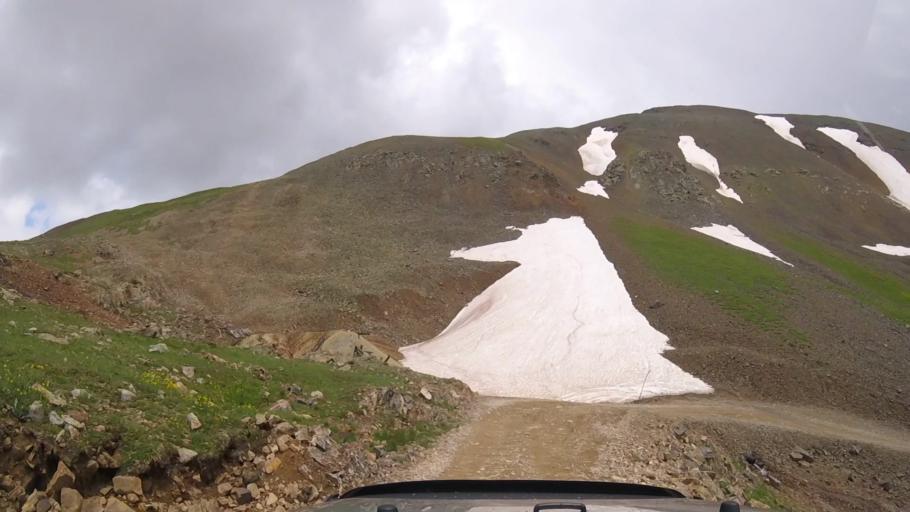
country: US
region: Colorado
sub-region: San Juan County
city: Silverton
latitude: 37.9165
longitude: -107.6273
